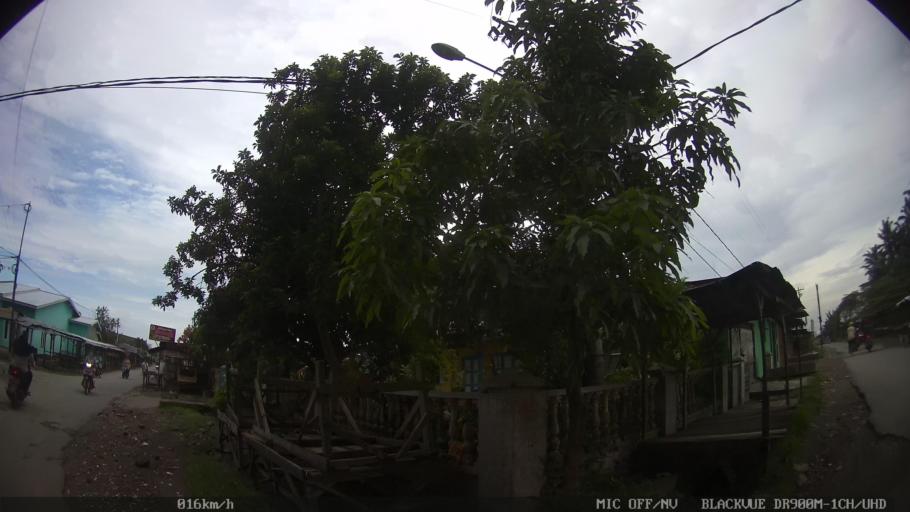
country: ID
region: North Sumatra
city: Sunggal
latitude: 3.5911
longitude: 98.5661
